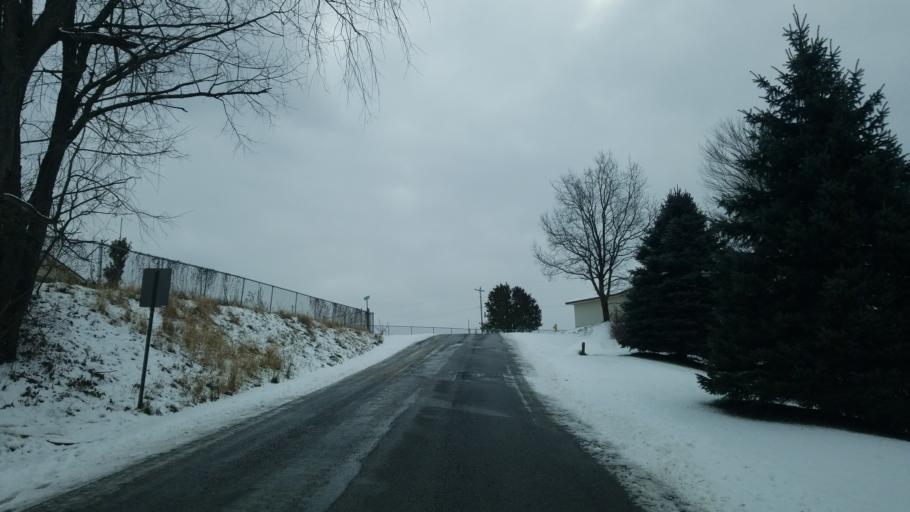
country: US
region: Pennsylvania
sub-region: Clearfield County
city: DuBois
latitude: 41.1115
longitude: -78.7303
